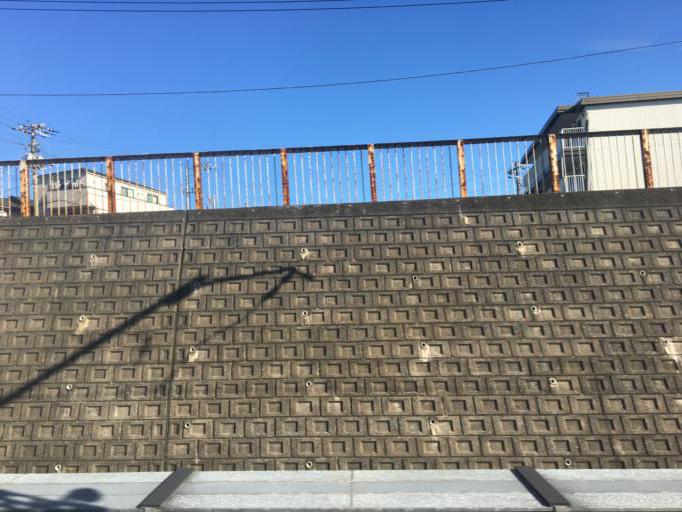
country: JP
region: Chiba
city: Funabashi
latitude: 35.7139
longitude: 139.9552
